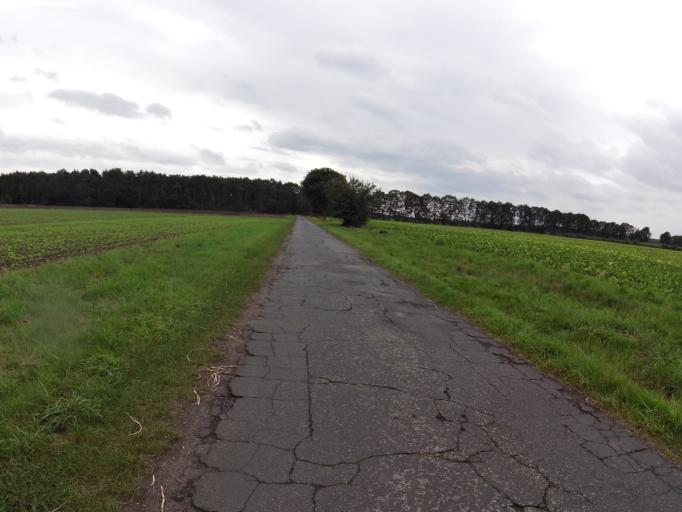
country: DE
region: Lower Saxony
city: Scheessel
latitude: 53.1502
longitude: 9.4506
